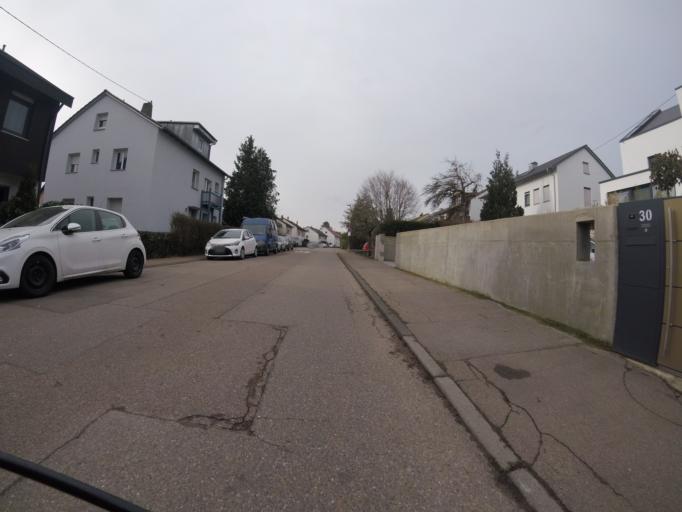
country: DE
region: Baden-Wuerttemberg
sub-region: Regierungsbezirk Stuttgart
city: Backnang
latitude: 48.9492
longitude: 9.4167
